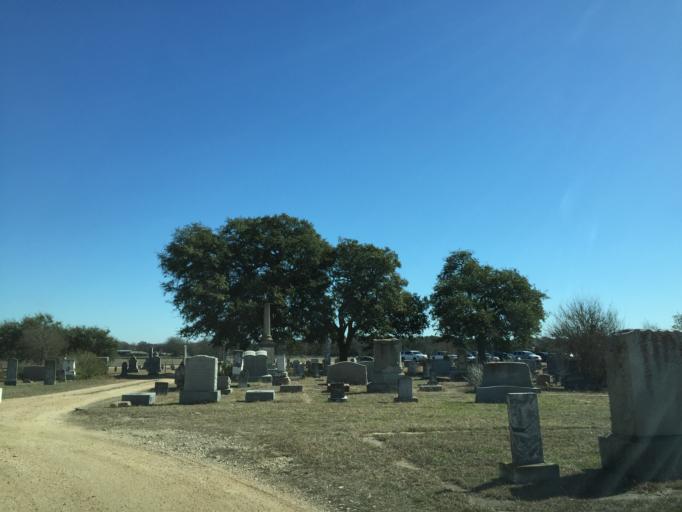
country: US
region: Texas
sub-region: Williamson County
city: Leander
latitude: 30.5765
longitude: -97.8695
